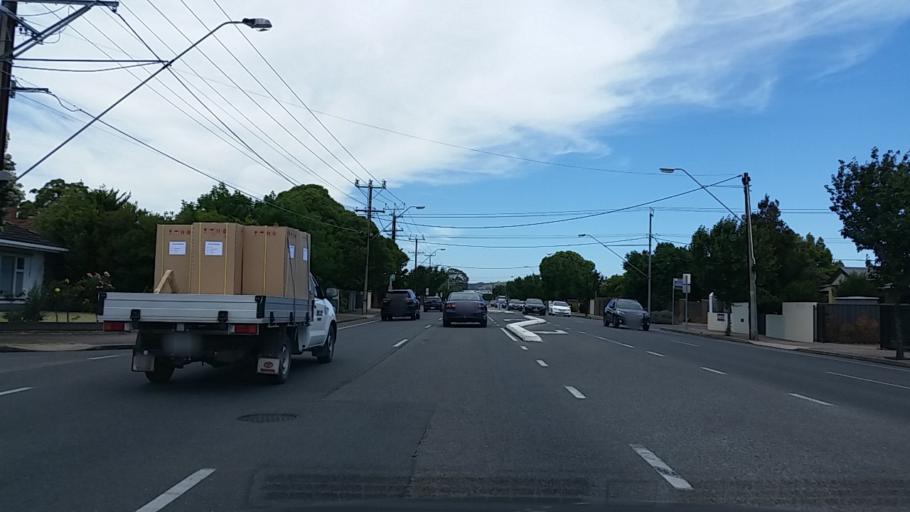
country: AU
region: South Australia
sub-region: Holdfast Bay
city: North Brighton
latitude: -35.0009
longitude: 138.5335
